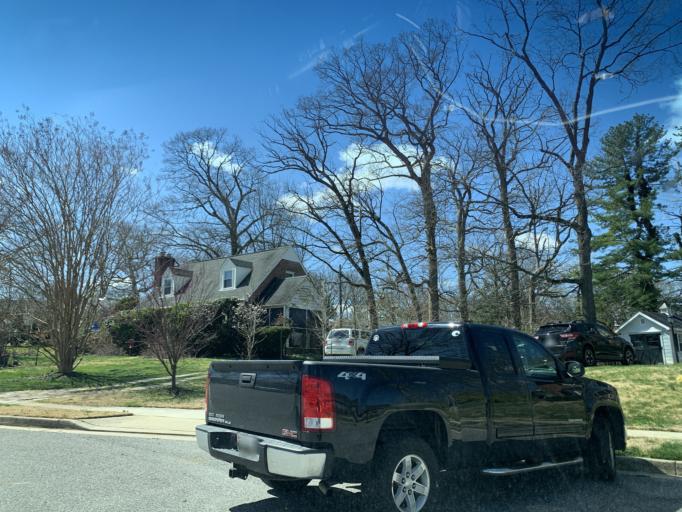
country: US
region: Maryland
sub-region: Baltimore County
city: Timonium
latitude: 39.4357
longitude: -76.6154
